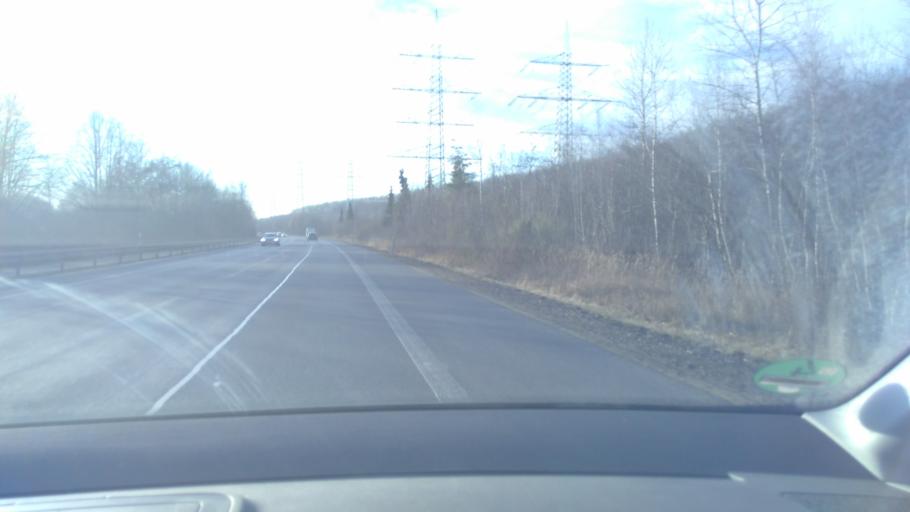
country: DE
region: North Rhine-Westphalia
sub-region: Regierungsbezirk Koln
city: Bergheim
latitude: 50.9728
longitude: 6.6478
